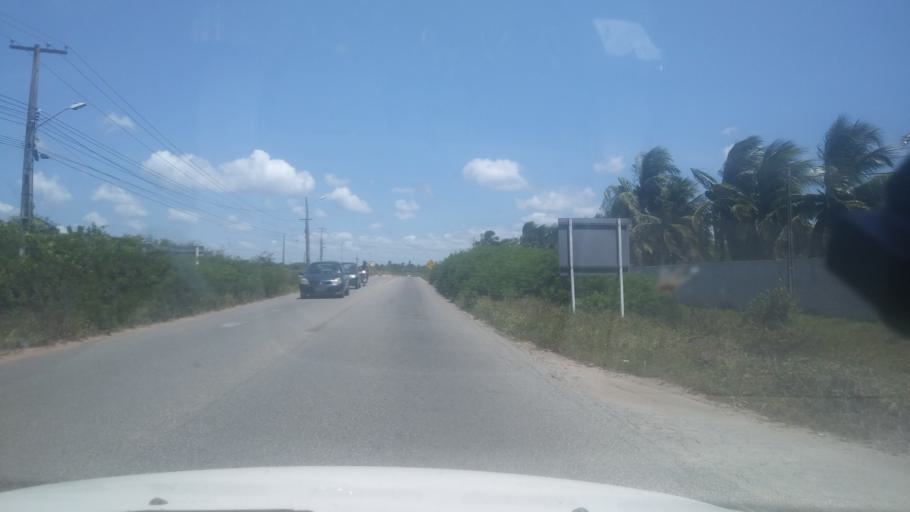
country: BR
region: Rio Grande do Norte
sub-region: Extremoz
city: Extremoz
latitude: -5.7195
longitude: -35.2777
